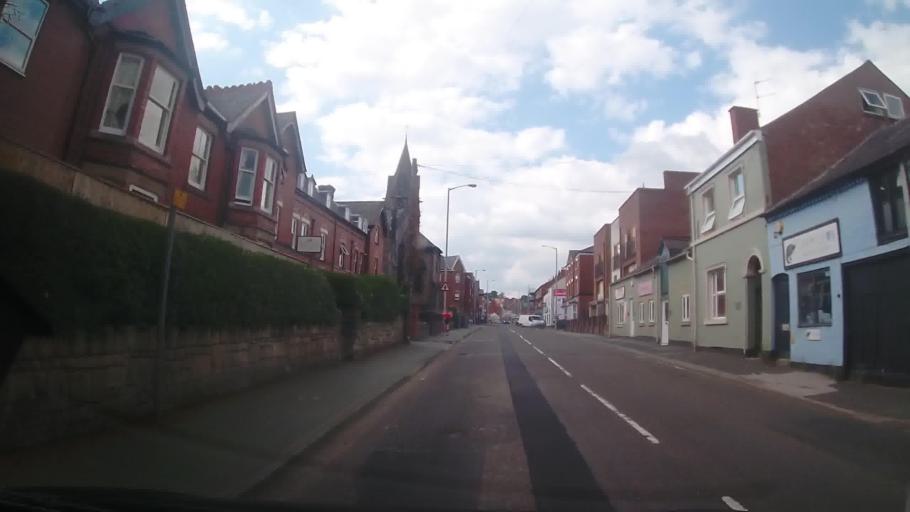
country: GB
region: England
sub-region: Shropshire
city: Oswestry
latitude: 52.8571
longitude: -3.0511
